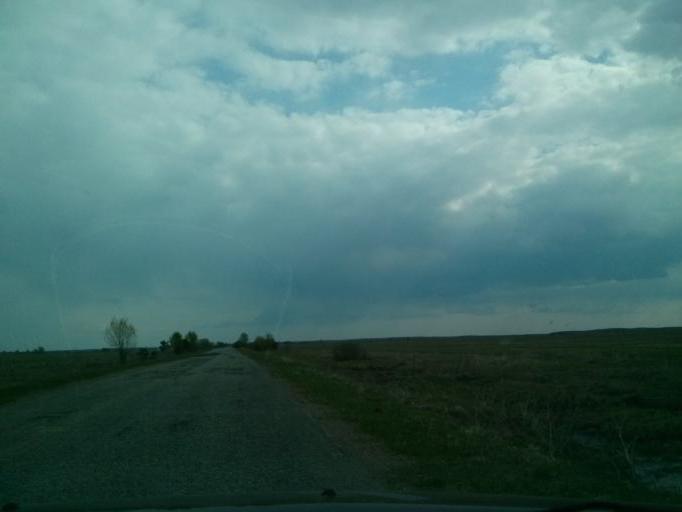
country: RU
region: Vladimir
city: Melenki
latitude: 55.3102
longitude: 41.7838
